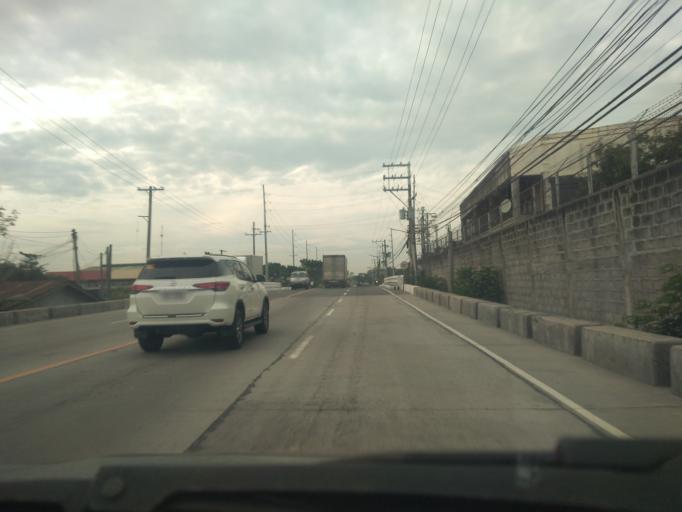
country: PH
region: Central Luzon
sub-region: Province of Pampanga
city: San Fernando
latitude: 15.0281
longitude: 120.6971
